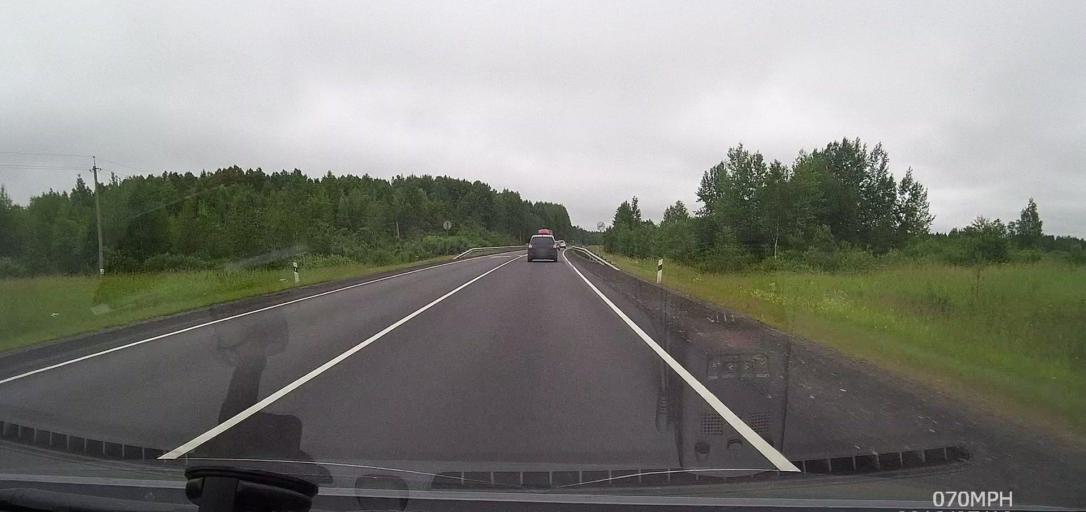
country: RU
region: Leningrad
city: Syas'stroy
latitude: 60.2749
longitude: 32.8011
